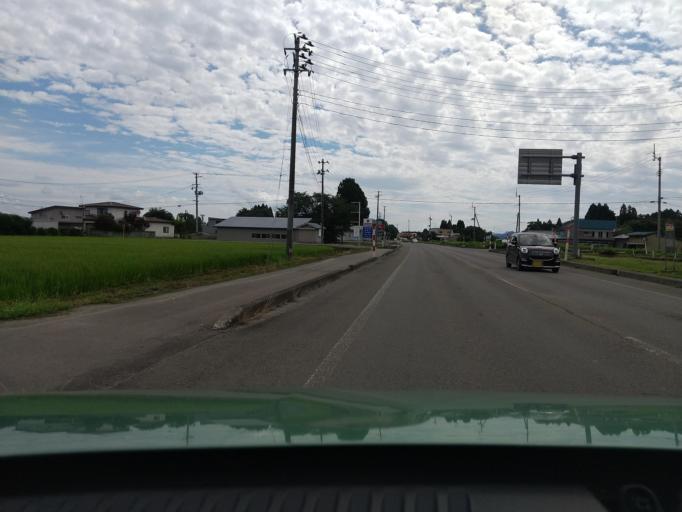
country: JP
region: Akita
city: Kakunodatemachi
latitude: 39.5746
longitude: 140.5640
